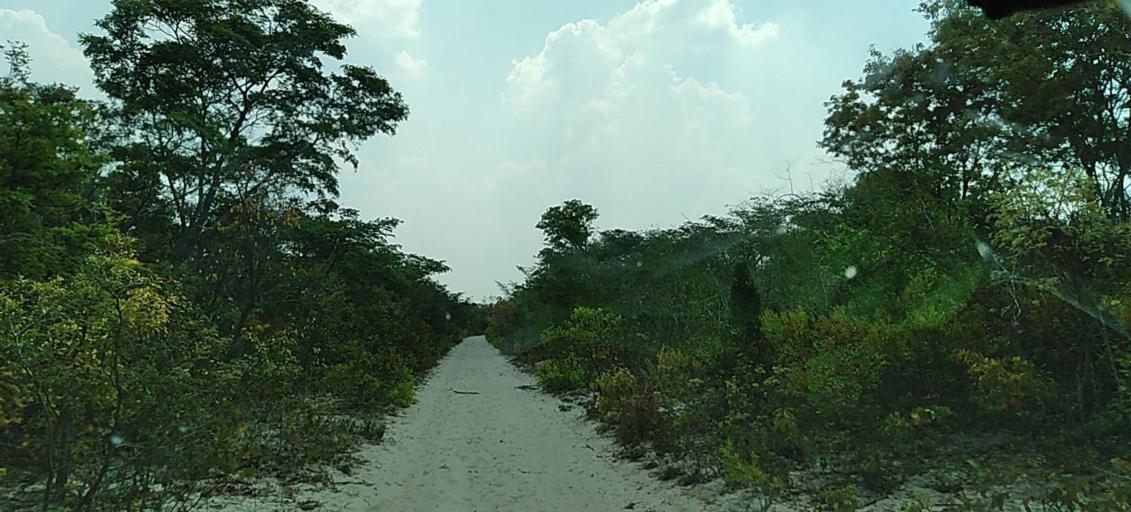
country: ZM
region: North-Western
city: Kabompo
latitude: -13.4008
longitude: 23.8134
